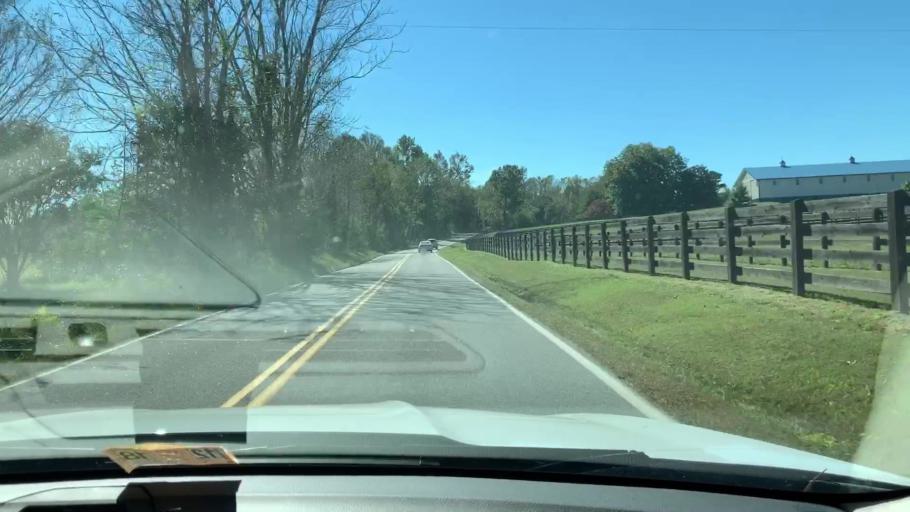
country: US
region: Virginia
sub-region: King William County
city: West Point
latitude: 37.4698
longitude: -76.8306
